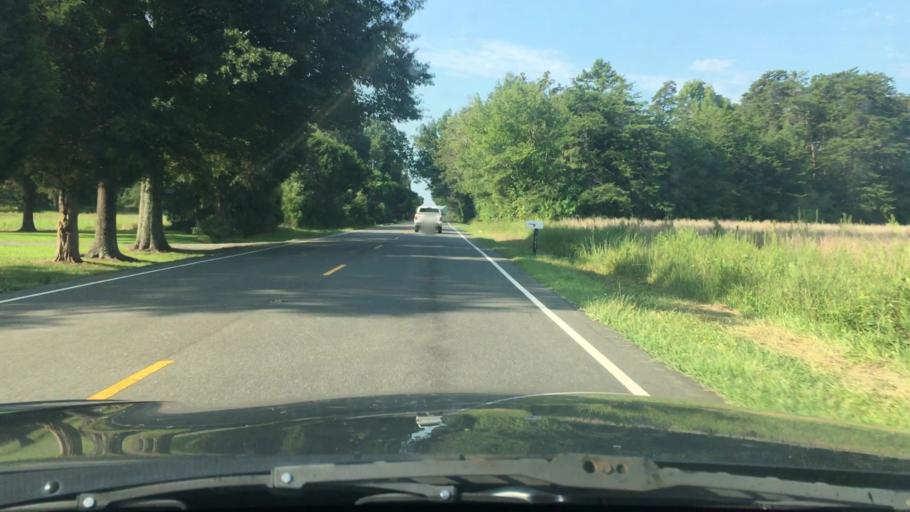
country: US
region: North Carolina
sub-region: Caswell County
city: Yanceyville
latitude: 36.3041
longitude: -79.3636
